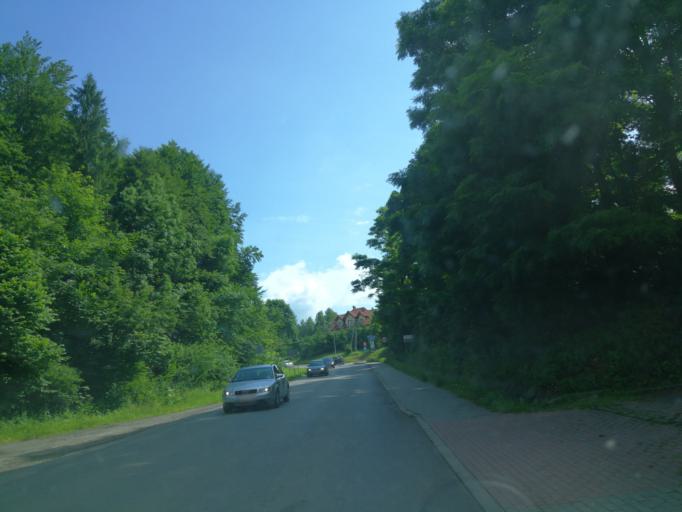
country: PL
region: Subcarpathian Voivodeship
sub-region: Powiat leski
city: Polanczyk
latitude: 49.3741
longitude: 22.4179
